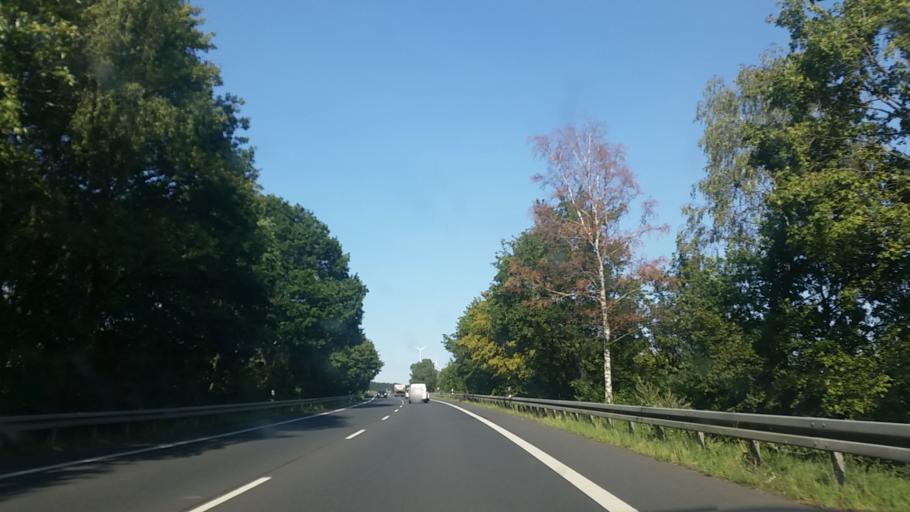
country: DE
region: Lower Saxony
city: Coppenbrugge
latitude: 52.1081
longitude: 9.4844
